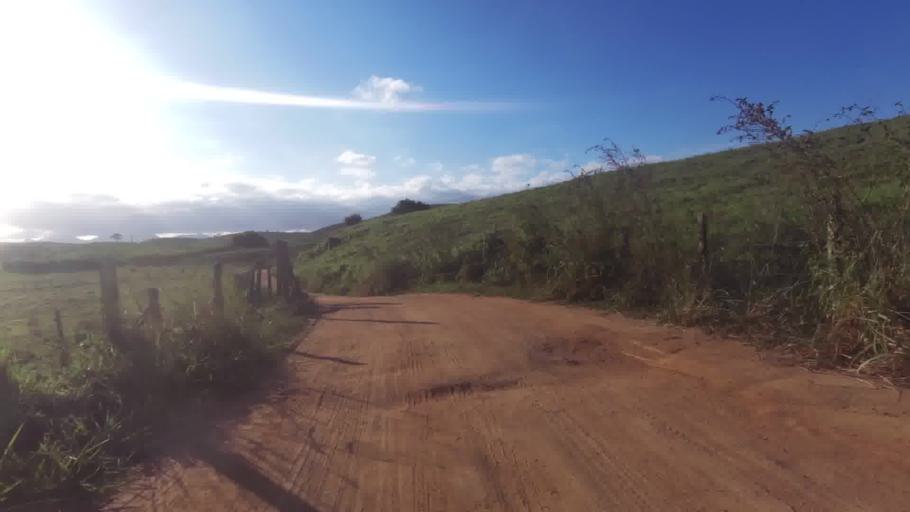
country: BR
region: Espirito Santo
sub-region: Marataizes
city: Marataizes
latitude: -21.1339
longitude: -41.0187
